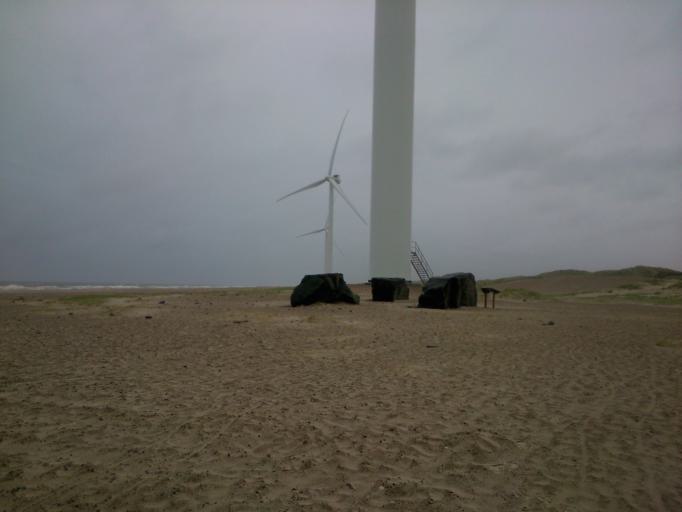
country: DK
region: Central Jutland
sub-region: Ringkobing-Skjern Kommune
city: Hvide Sande
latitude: 56.0008
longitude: 8.1135
